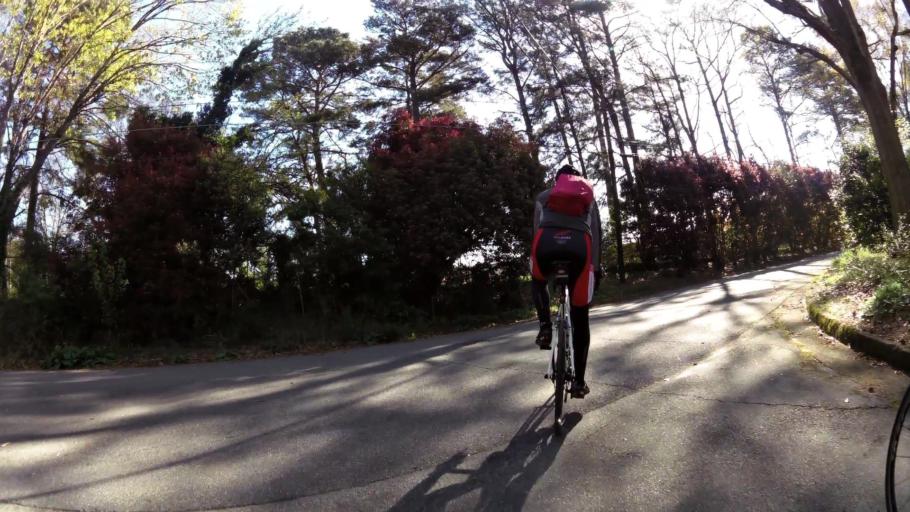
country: US
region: Georgia
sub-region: DeKalb County
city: Clarkston
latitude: 33.8313
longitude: -84.2659
